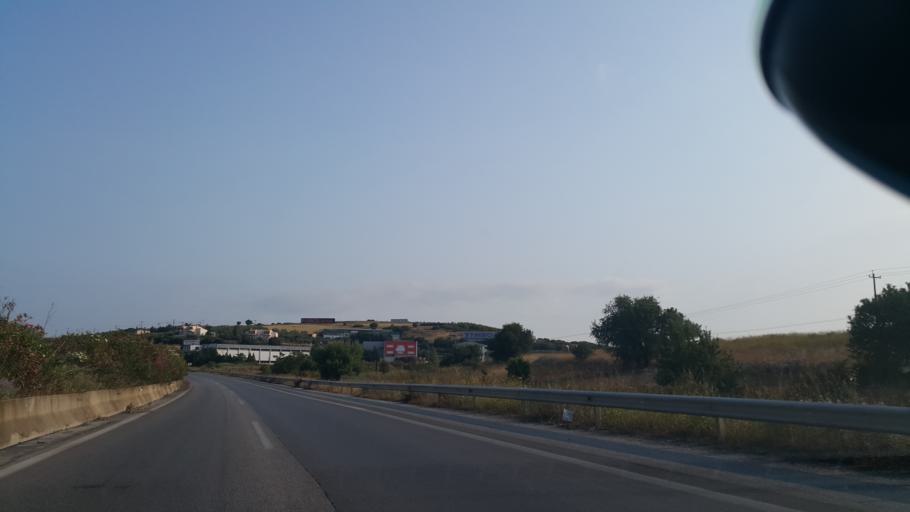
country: GR
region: Central Macedonia
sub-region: Nomos Thessalonikis
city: Kato Scholari
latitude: 40.4470
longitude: 23.0109
